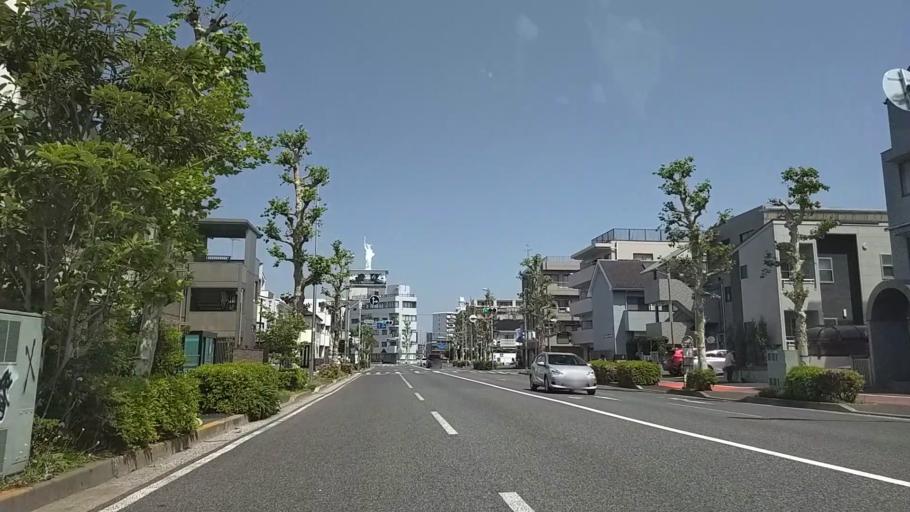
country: JP
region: Kanagawa
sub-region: Kawasaki-shi
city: Kawasaki
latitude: 35.5158
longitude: 139.6901
